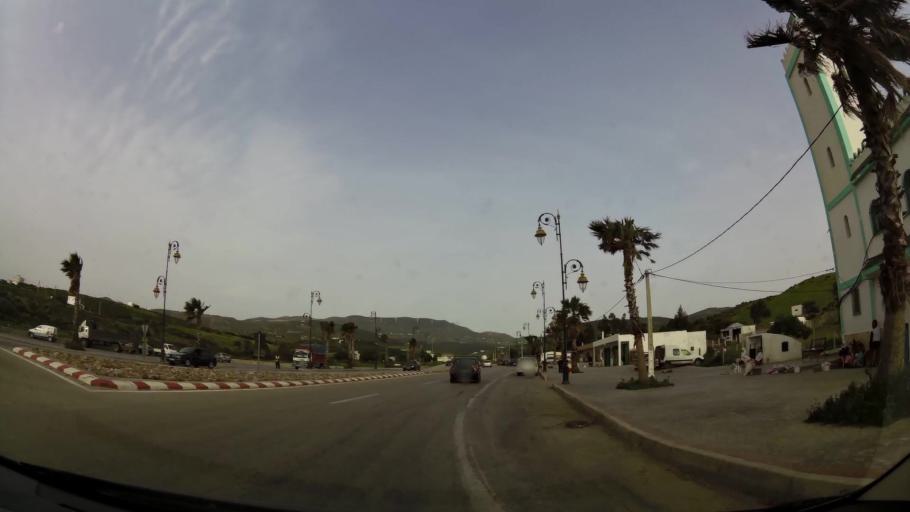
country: MA
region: Tanger-Tetouan
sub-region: Tanger-Assilah
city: Dar Chaoui
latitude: 35.5682
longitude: -5.6166
